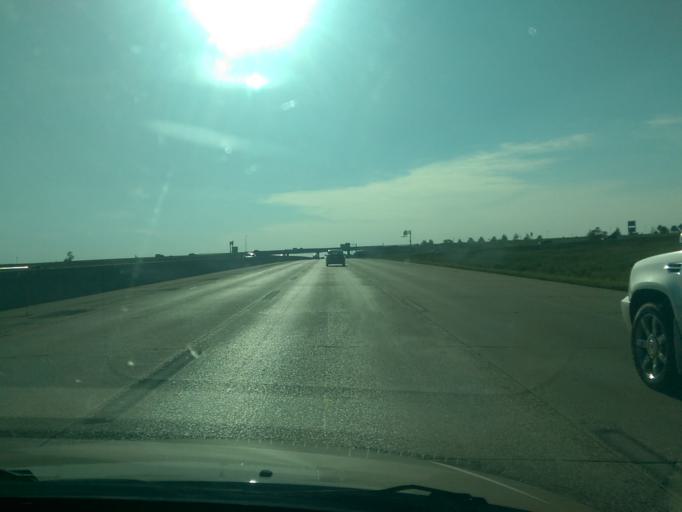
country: US
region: Missouri
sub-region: Jackson County
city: East Independence
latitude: 39.0413
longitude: -94.3577
